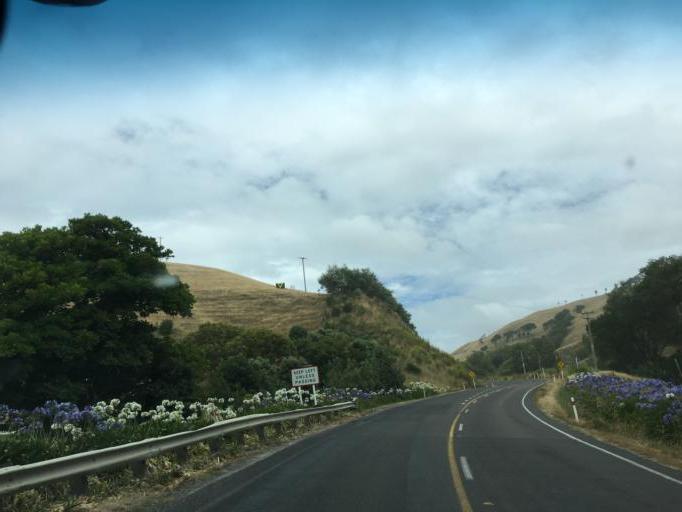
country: NZ
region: Gisborne
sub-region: Gisborne District
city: Gisborne
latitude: -38.6463
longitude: 178.1442
